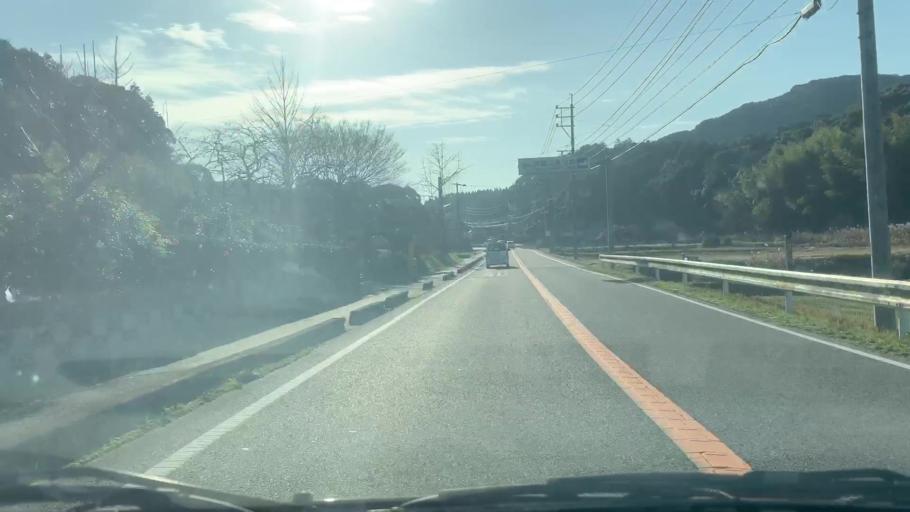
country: JP
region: Saga Prefecture
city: Takeocho-takeo
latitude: 33.2470
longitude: 130.0045
